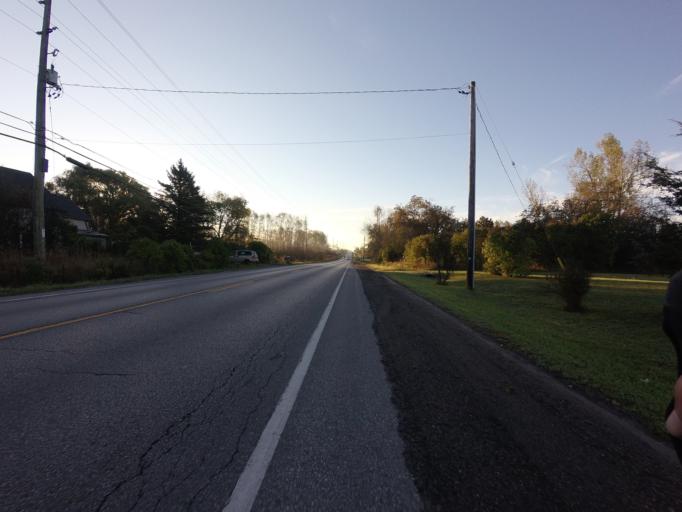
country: CA
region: Ontario
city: Quinte West
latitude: 44.0291
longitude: -77.5502
